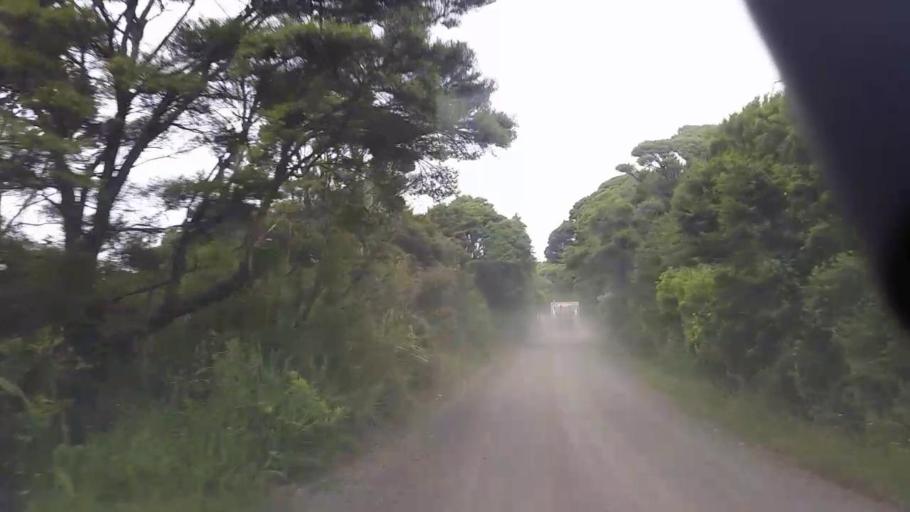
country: NZ
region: Auckland
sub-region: Auckland
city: Muriwai Beach
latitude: -36.9270
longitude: 174.4863
